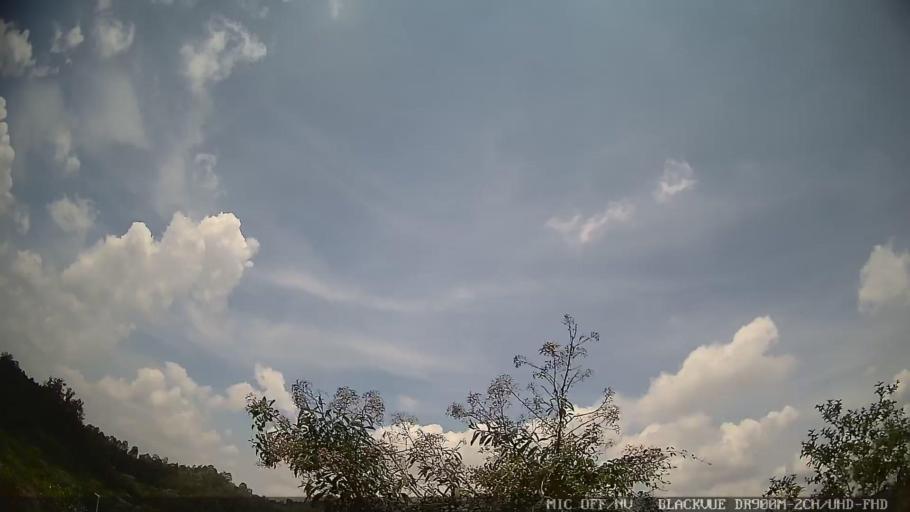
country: BR
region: Sao Paulo
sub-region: Itatiba
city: Itatiba
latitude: -23.0080
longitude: -46.9002
